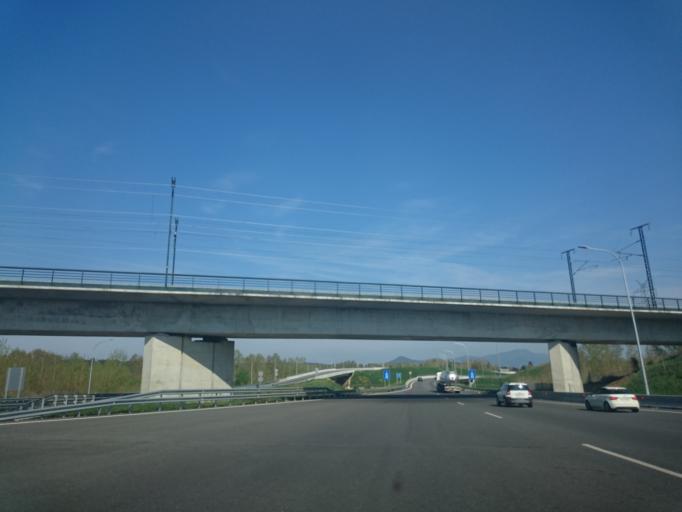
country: ES
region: Catalonia
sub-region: Provincia de Girona
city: Fornells de la Selva
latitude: 41.9294
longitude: 2.7898
